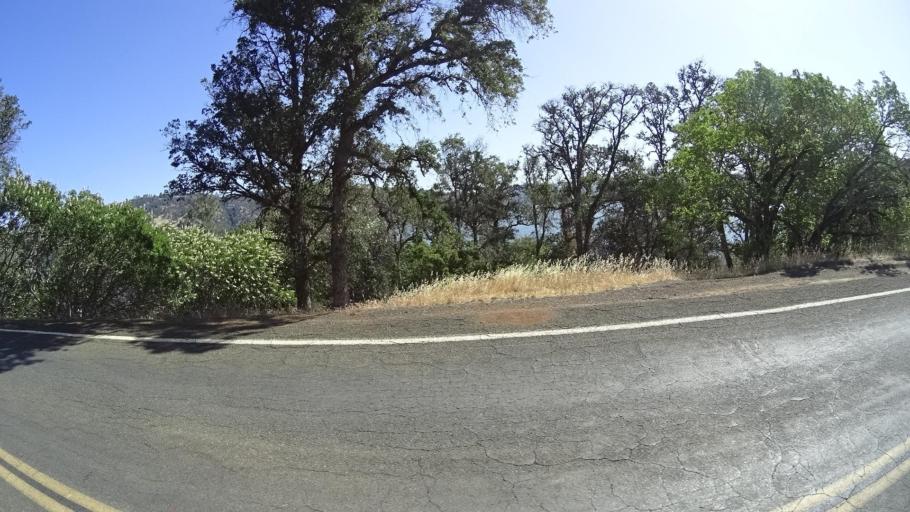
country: US
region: California
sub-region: Lake County
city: Clearlake Oaks
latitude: 39.0043
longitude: -122.7107
